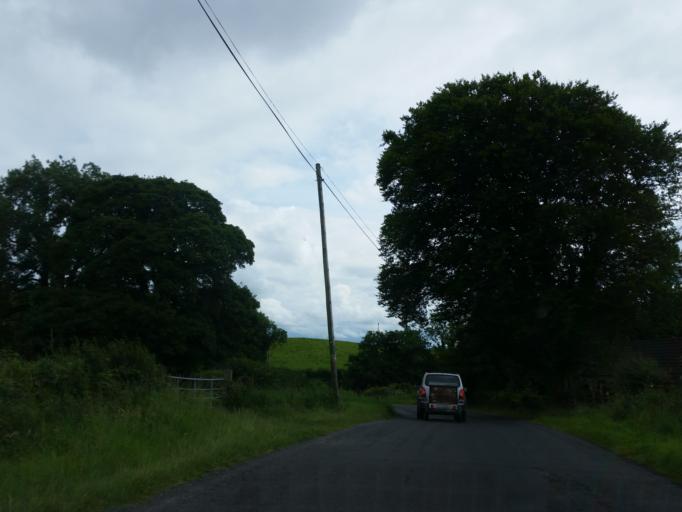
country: IE
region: Ulster
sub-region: County Monaghan
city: Clones
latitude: 54.2065
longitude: -7.2435
